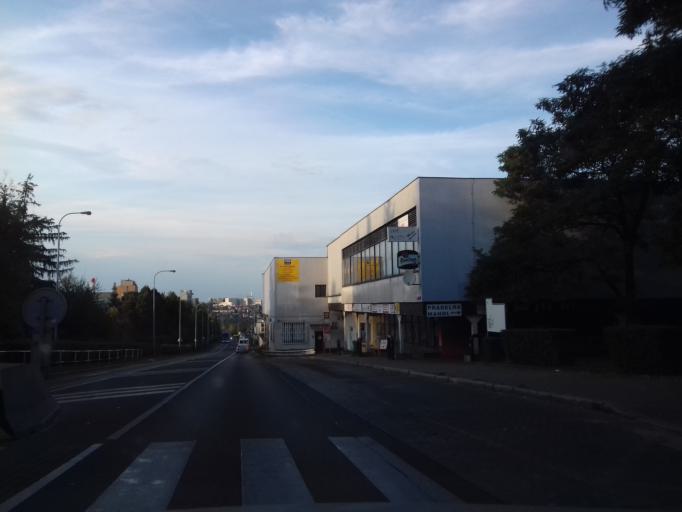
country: CZ
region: Praha
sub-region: Praha 4
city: Hodkovicky
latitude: 50.0229
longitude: 14.4515
